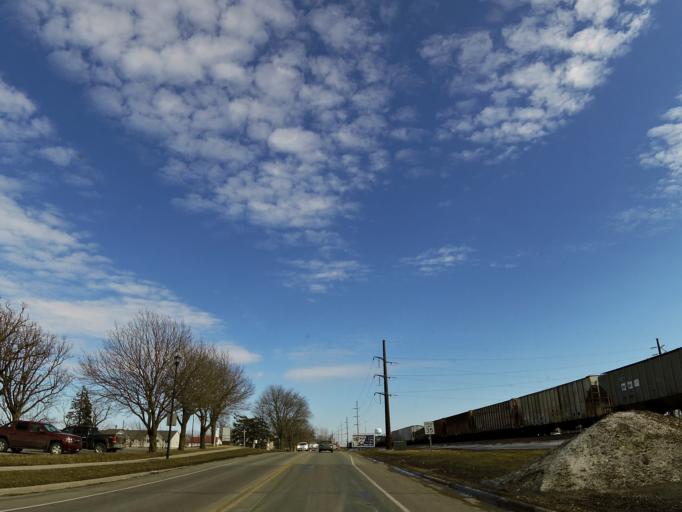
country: US
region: Minnesota
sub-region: Waseca County
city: Waseca
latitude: 44.0784
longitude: -93.5221
